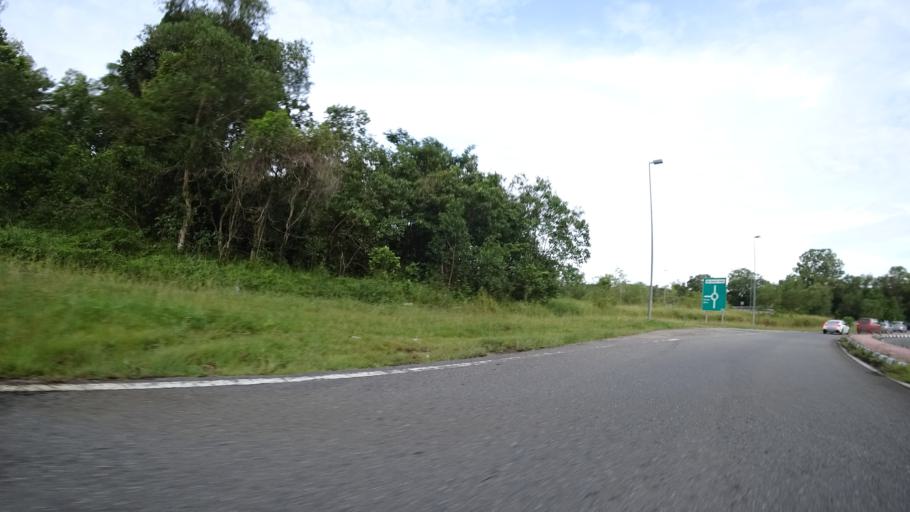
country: BN
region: Brunei and Muara
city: Bandar Seri Begawan
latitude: 4.9457
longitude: 114.9374
